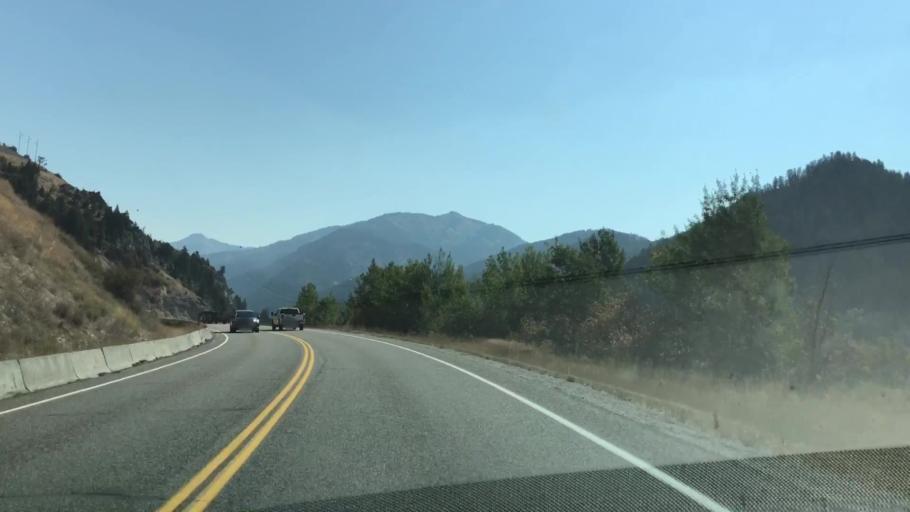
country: US
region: Idaho
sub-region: Teton County
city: Victor
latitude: 43.3188
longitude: -111.1530
